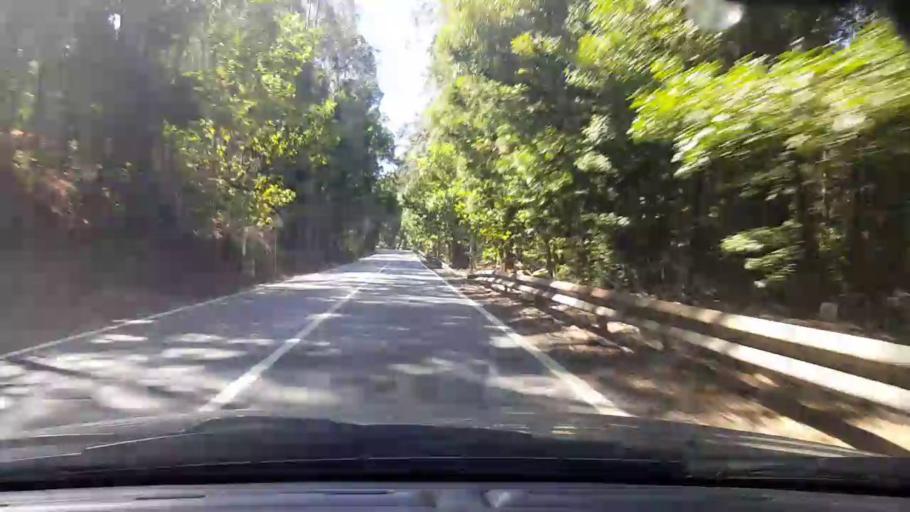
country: PT
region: Braga
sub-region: Vila Nova de Famalicao
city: Ribeirao
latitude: 41.3402
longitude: -8.6262
